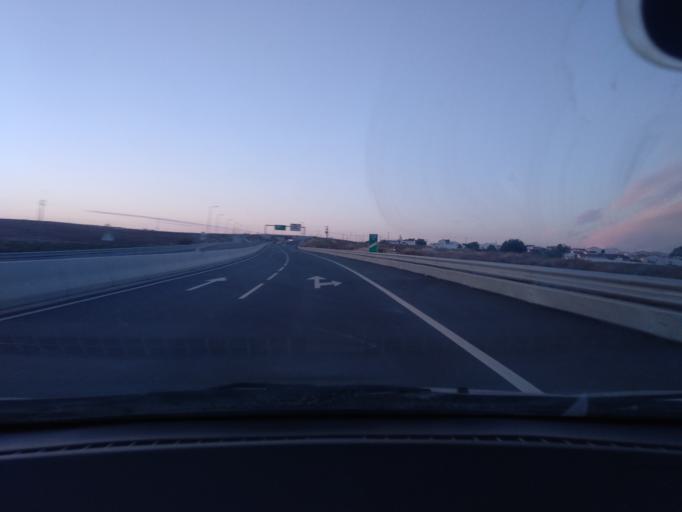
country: PT
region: Beja
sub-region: Beja
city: Beja
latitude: 37.9664
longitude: -7.8752
